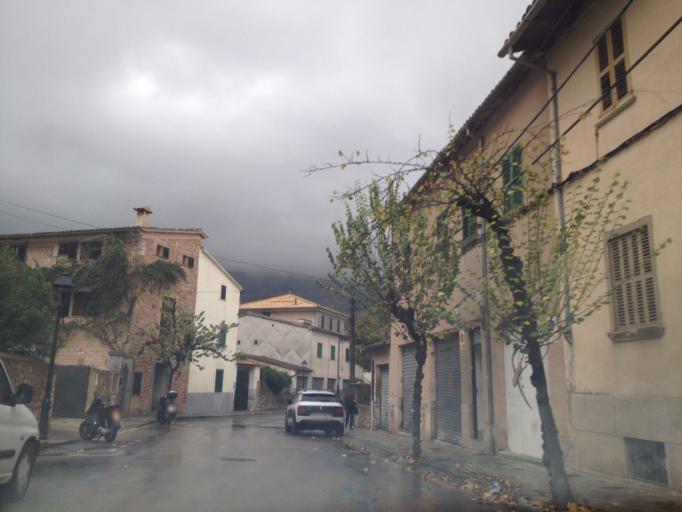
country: ES
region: Balearic Islands
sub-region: Illes Balears
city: Soller
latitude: 39.7709
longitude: 2.7170
